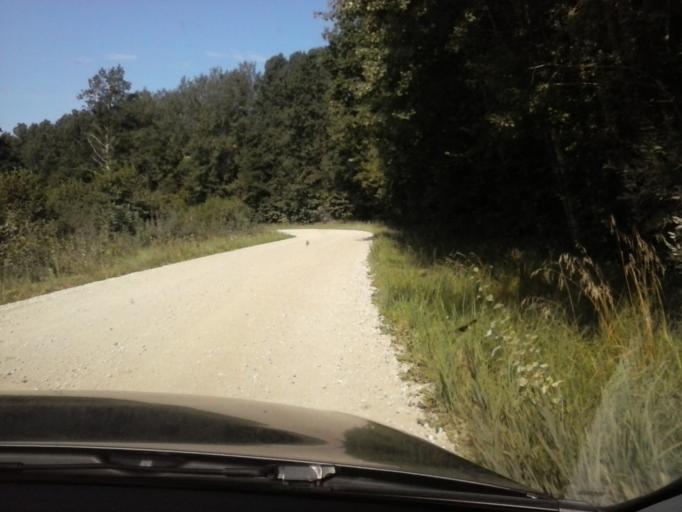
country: EE
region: Laeaene
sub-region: Ridala Parish
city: Uuemoisa
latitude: 58.8836
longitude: 23.5774
